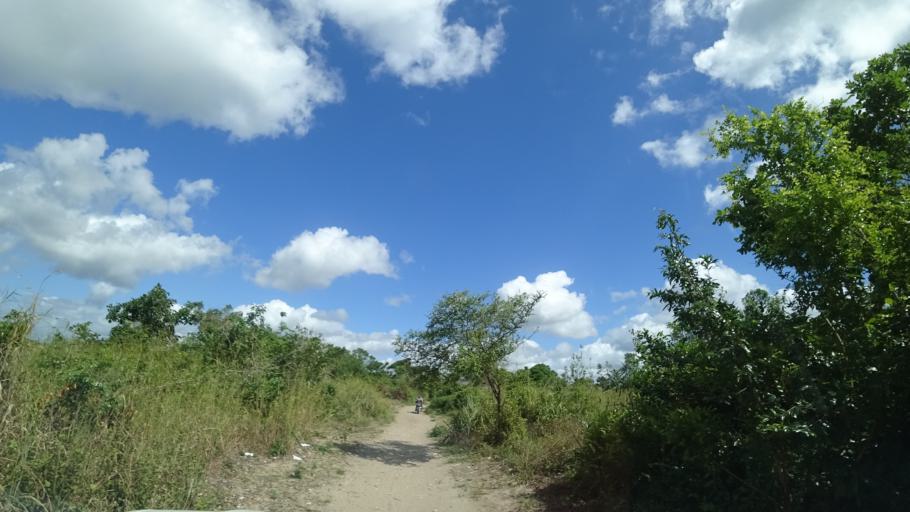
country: MZ
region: Sofala
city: Dondo
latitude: -19.3599
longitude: 34.5761
